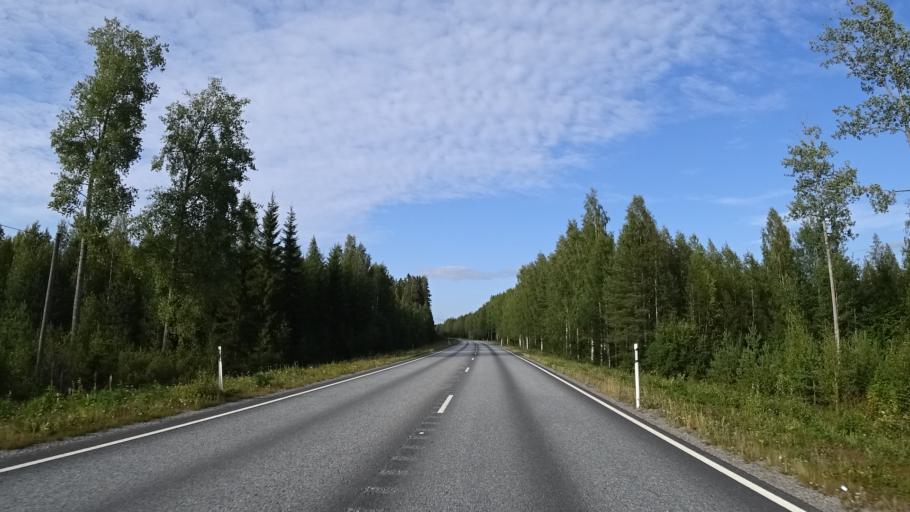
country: FI
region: North Karelia
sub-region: Joensuu
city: Eno
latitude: 62.8195
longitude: 30.1882
